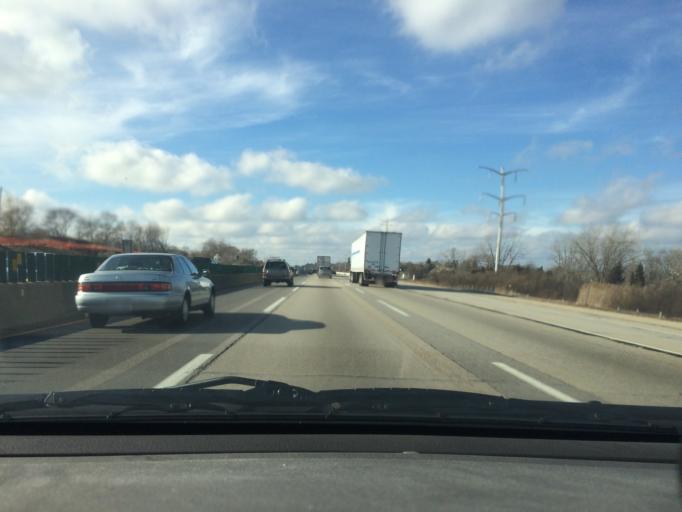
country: US
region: Illinois
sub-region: Cook County
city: Hoffman Estates
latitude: 42.0651
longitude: -88.0884
